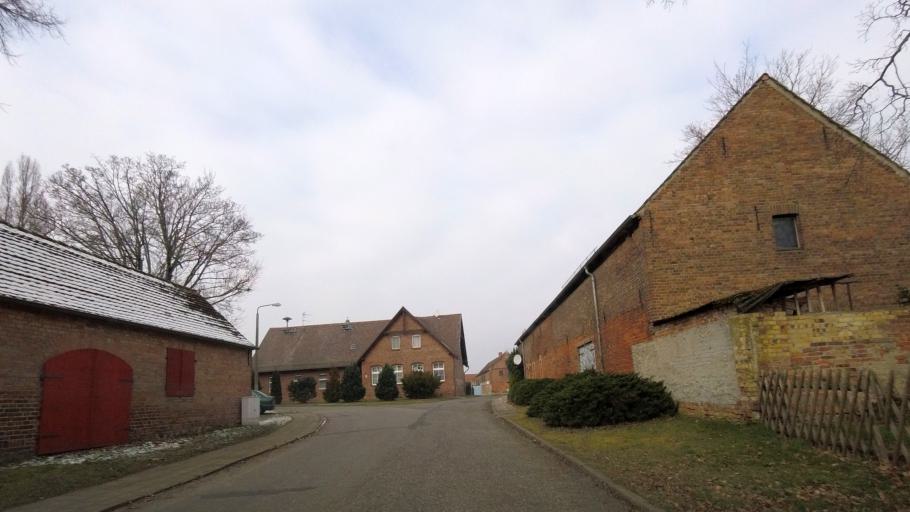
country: DE
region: Brandenburg
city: Juterbog
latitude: 51.9476
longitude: 13.0870
